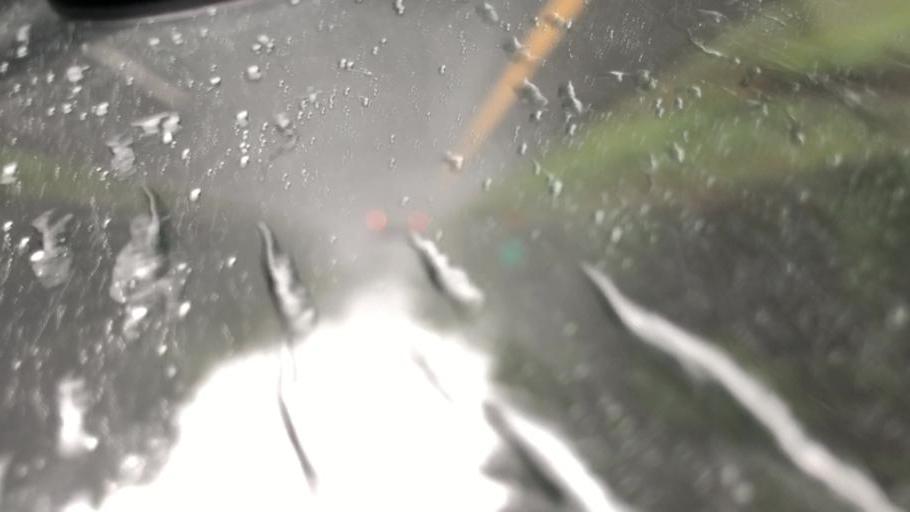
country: US
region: Massachusetts
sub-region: Hampden County
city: Westfield
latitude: 42.1562
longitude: -72.7945
